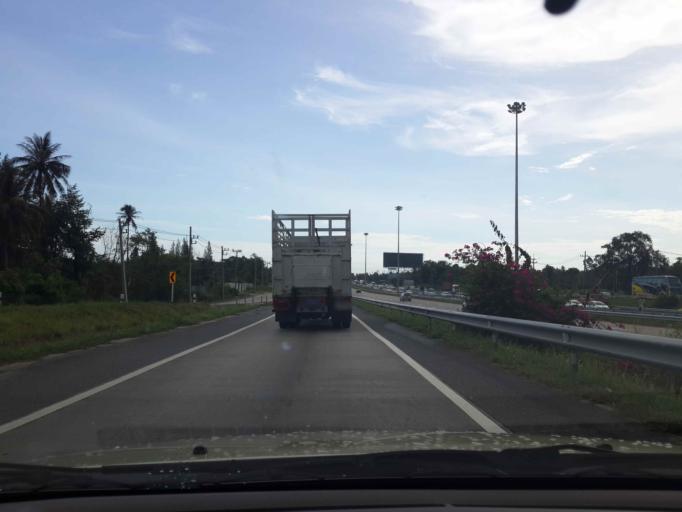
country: TH
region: Chon Buri
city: Bang Lamung
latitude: 12.9688
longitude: 100.9811
